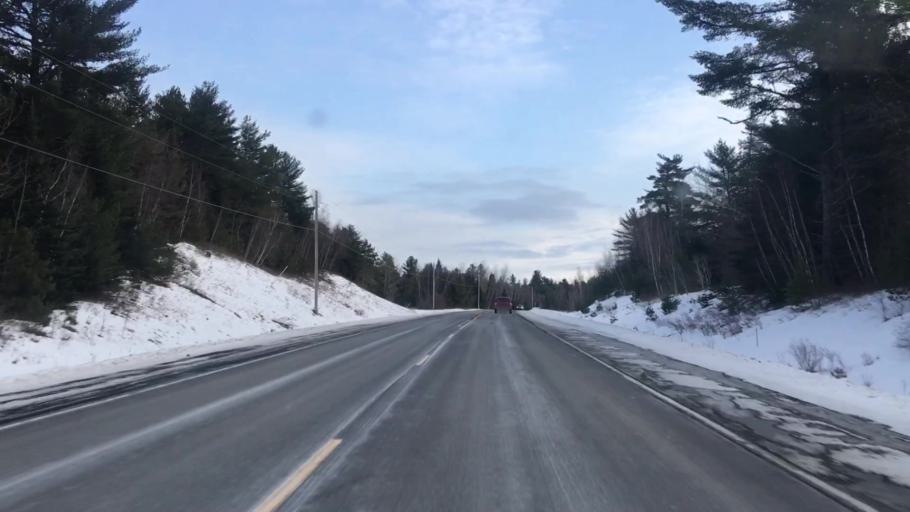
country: US
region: Maine
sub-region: Washington County
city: Addison
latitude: 44.9386
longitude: -67.7324
